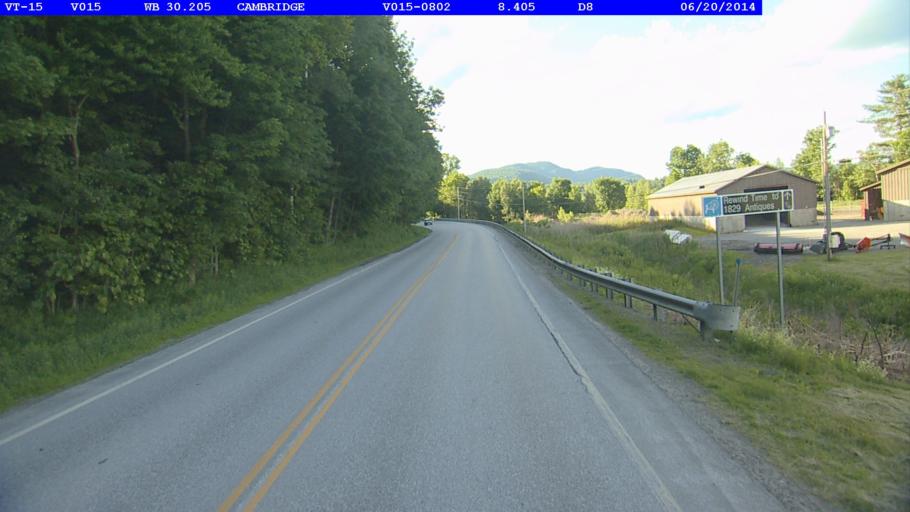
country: US
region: Vermont
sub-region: Lamoille County
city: Johnson
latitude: 44.6637
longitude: -72.7747
